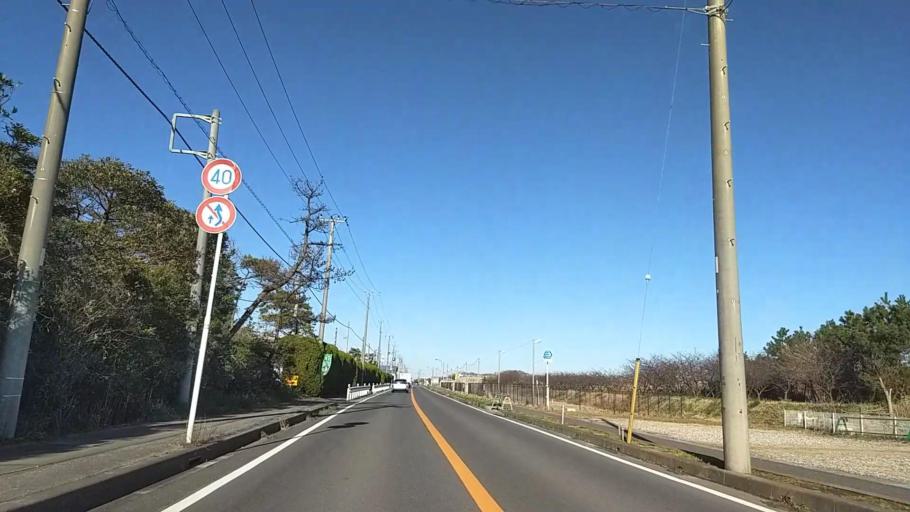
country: JP
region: Chiba
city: Togane
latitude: 35.4588
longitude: 140.4066
